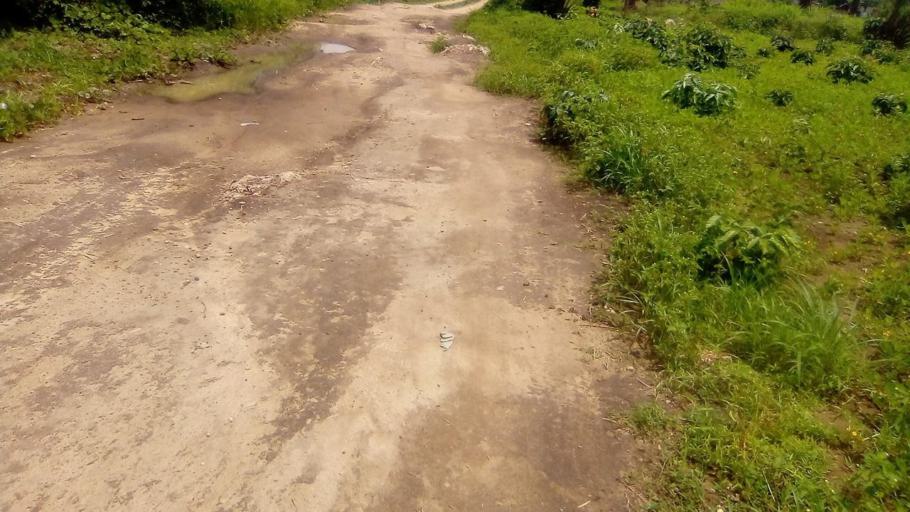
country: SL
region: Southern Province
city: Bo
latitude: 7.9344
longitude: -11.7467
